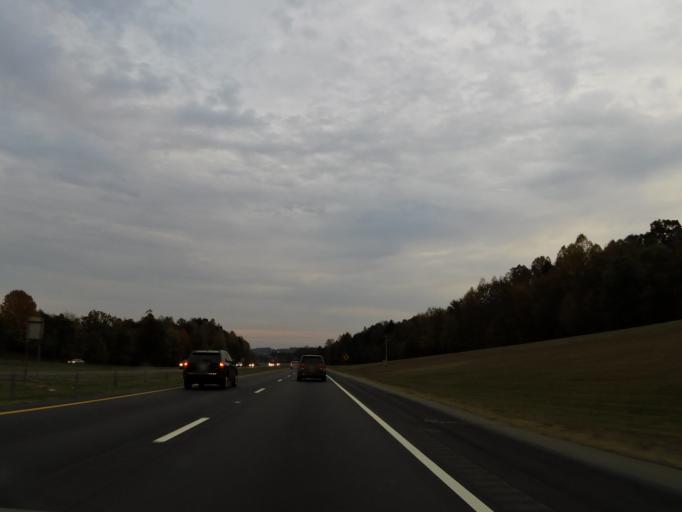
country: US
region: North Carolina
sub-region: Catawba County
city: Hickory
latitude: 35.7212
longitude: -81.3562
